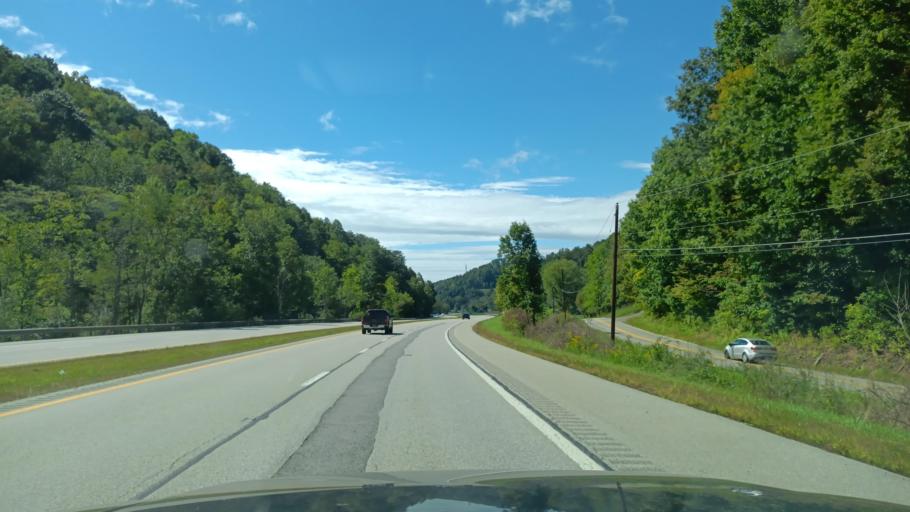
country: US
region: West Virginia
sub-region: Harrison County
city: Salem
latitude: 39.2971
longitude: -80.6198
